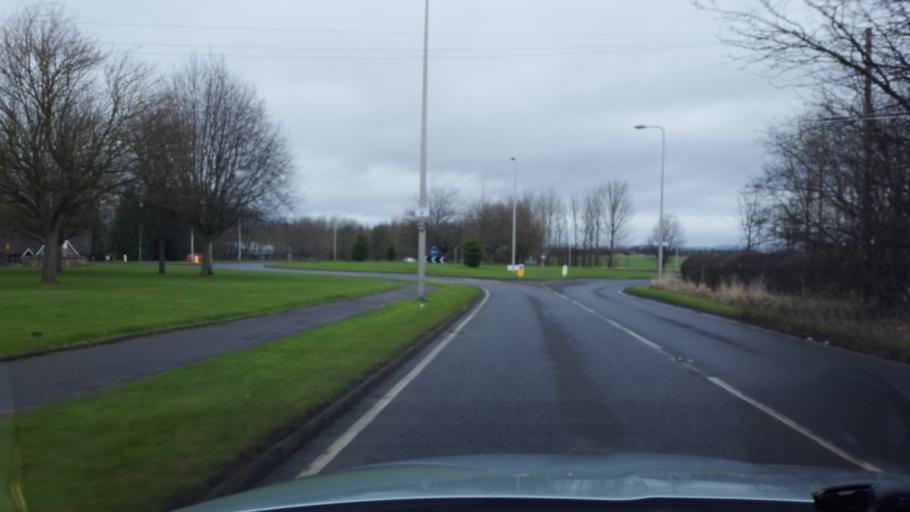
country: GB
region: Scotland
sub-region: Edinburgh
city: Currie
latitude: 55.9113
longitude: -3.3121
